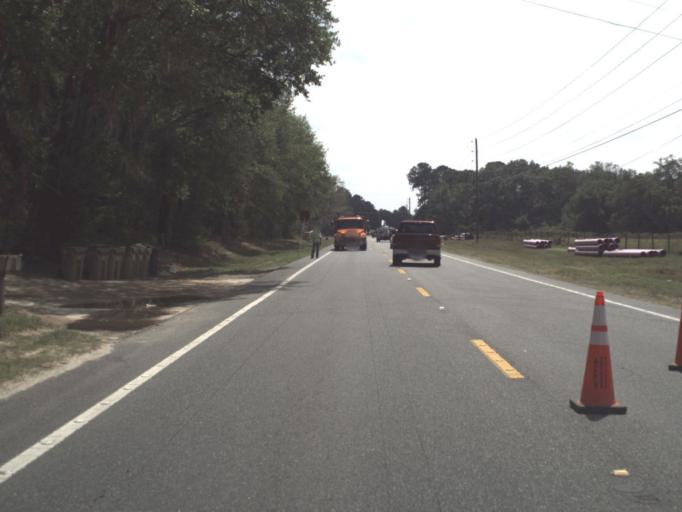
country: US
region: Florida
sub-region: Lake County
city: Groveland
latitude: 28.6232
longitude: -81.8250
